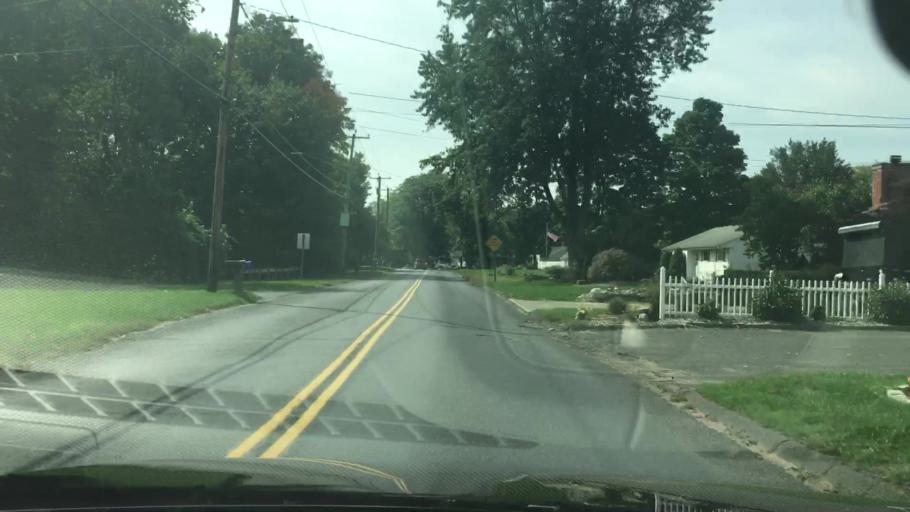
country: US
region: Connecticut
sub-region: Hartford County
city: Broad Brook
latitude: 41.8644
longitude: -72.5755
